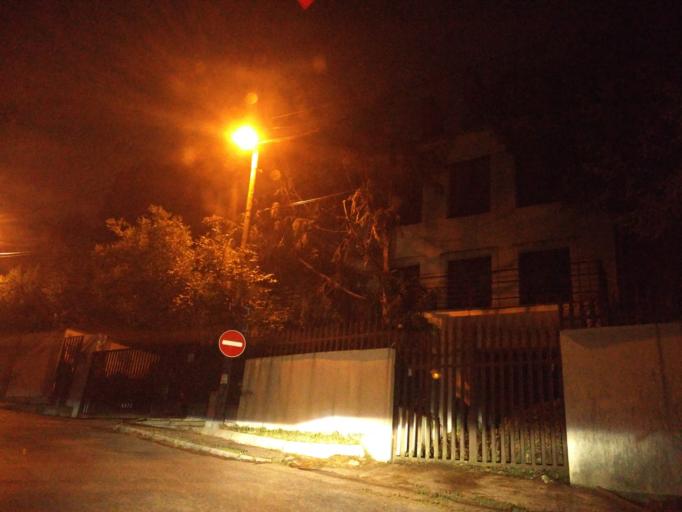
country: HU
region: Budapest
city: Budapest XII. keruelet
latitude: 47.5137
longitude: 18.9871
